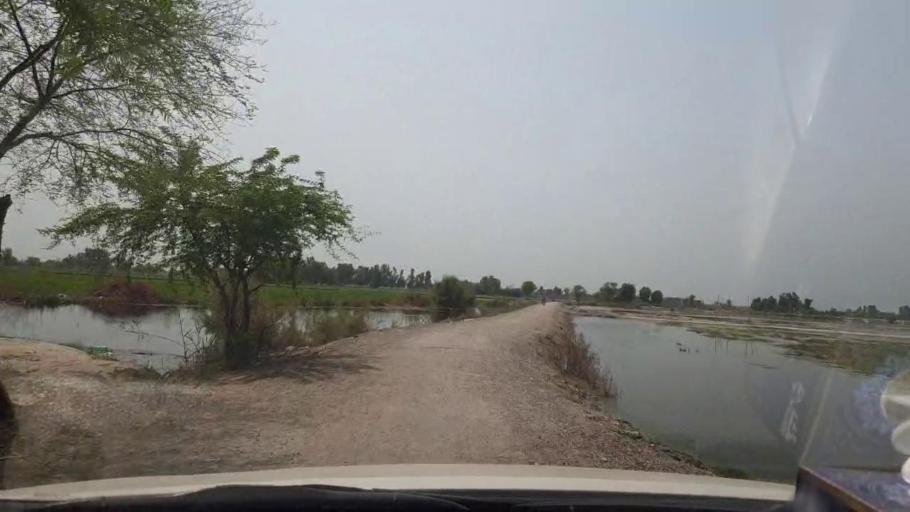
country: PK
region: Sindh
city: Shikarpur
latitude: 27.9869
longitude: 68.7063
